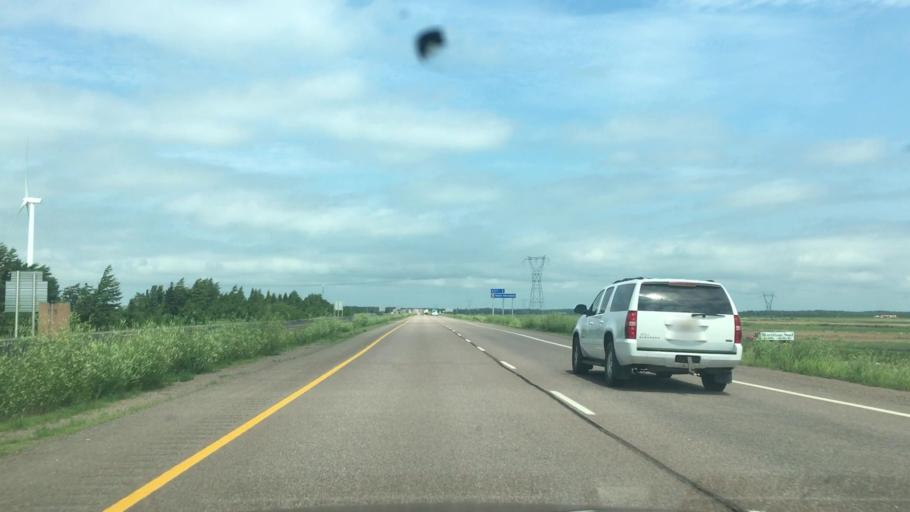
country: CA
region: Nova Scotia
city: Amherst
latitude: 45.8264
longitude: -64.2377
